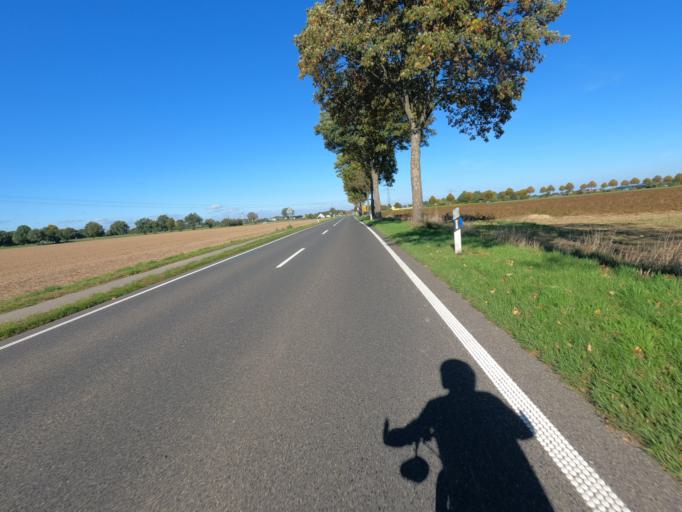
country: DE
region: North Rhine-Westphalia
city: Erkelenz
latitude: 51.0565
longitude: 6.3259
